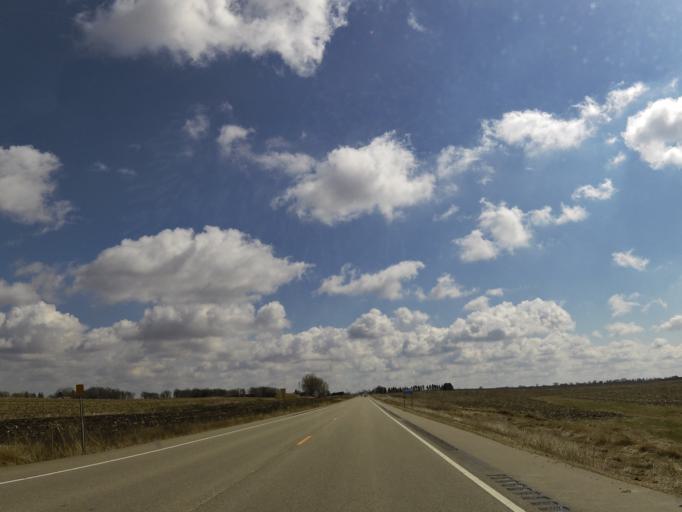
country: US
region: Minnesota
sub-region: Goodhue County
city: Kenyon
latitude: 44.1752
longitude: -92.9057
